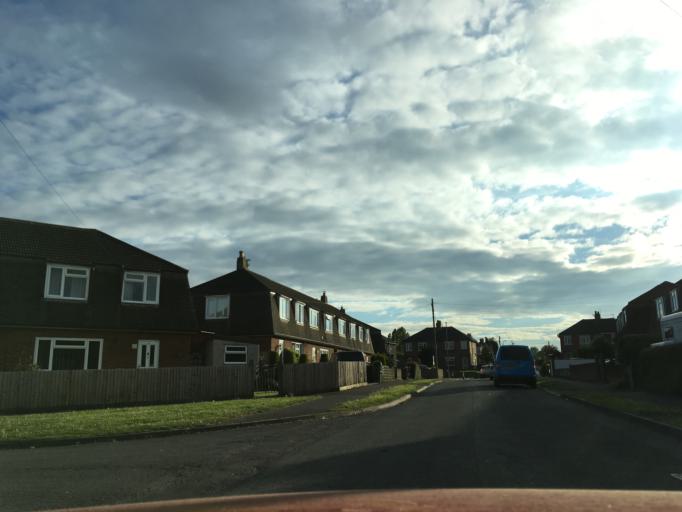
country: GB
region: Wales
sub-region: Monmouthshire
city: Chepstow
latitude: 51.6330
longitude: -2.6743
